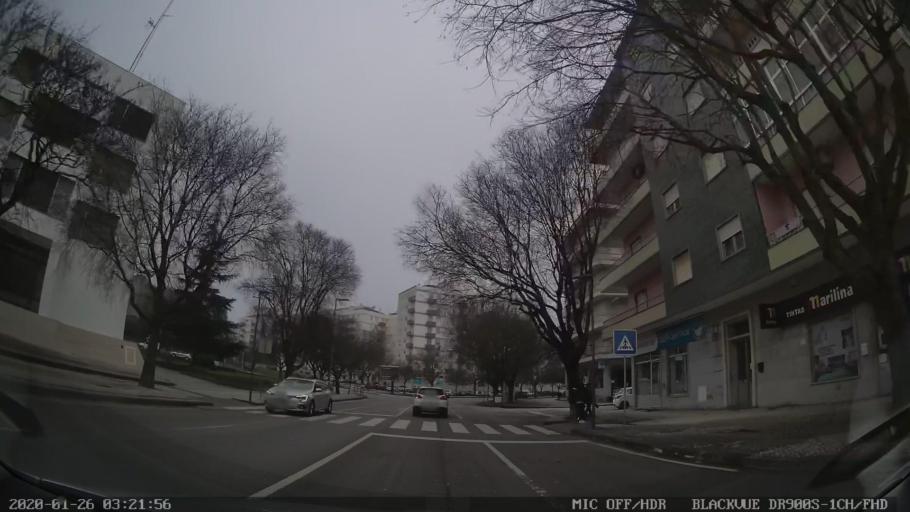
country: PT
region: Santarem
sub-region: Santarem
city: Santarem
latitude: 39.2274
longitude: -8.6878
